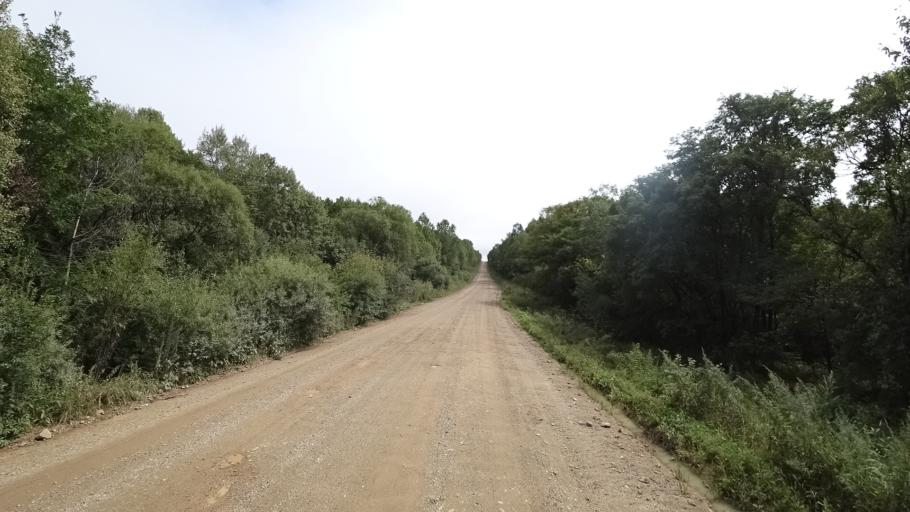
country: RU
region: Primorskiy
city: Lyalichi
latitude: 44.0981
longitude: 132.4289
